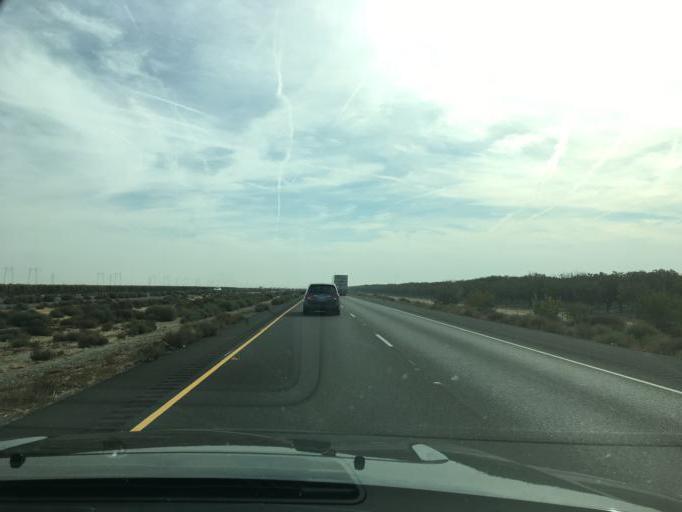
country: US
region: California
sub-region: Kings County
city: Kettleman City
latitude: 35.9139
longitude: -119.8912
